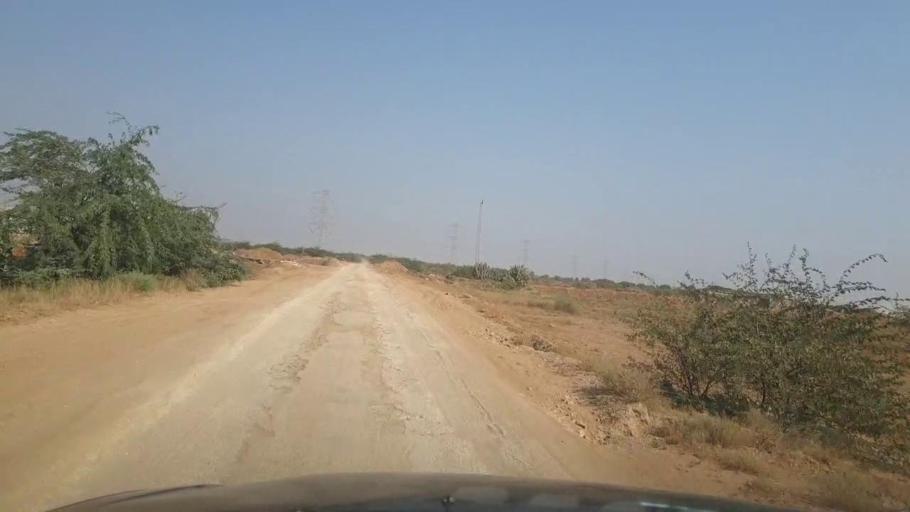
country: PK
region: Sindh
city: Gharo
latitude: 25.2298
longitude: 67.6776
